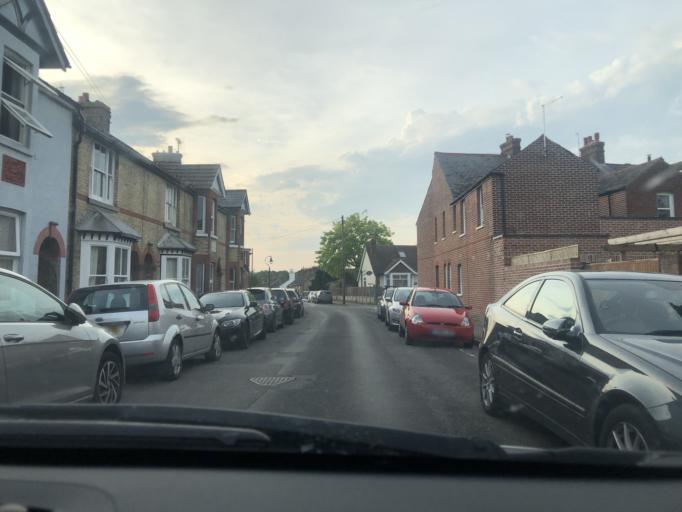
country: GB
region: England
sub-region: Kent
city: Canterbury
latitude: 51.2712
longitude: 1.0746
